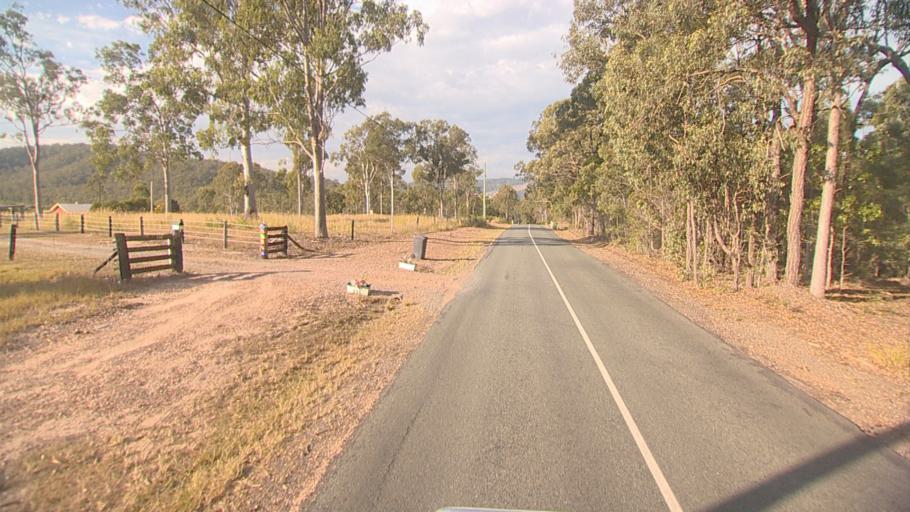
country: AU
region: Queensland
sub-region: Gold Coast
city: Ormeau Hills
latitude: -27.8453
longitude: 153.1501
